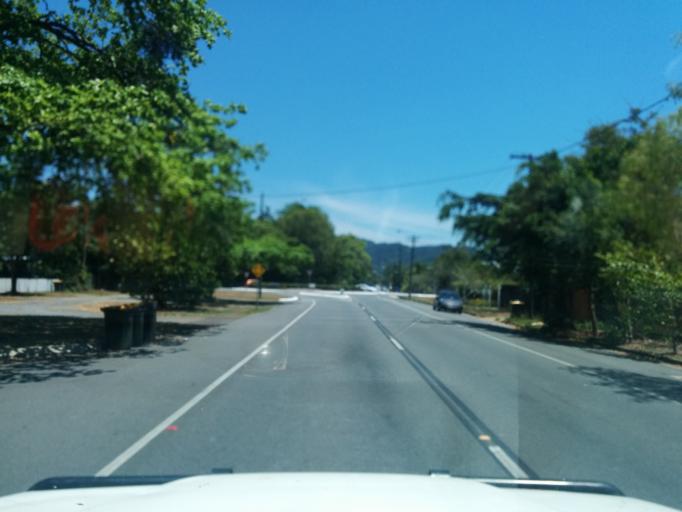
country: AU
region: Queensland
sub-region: Cairns
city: Cairns
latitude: -16.9192
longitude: 145.7594
